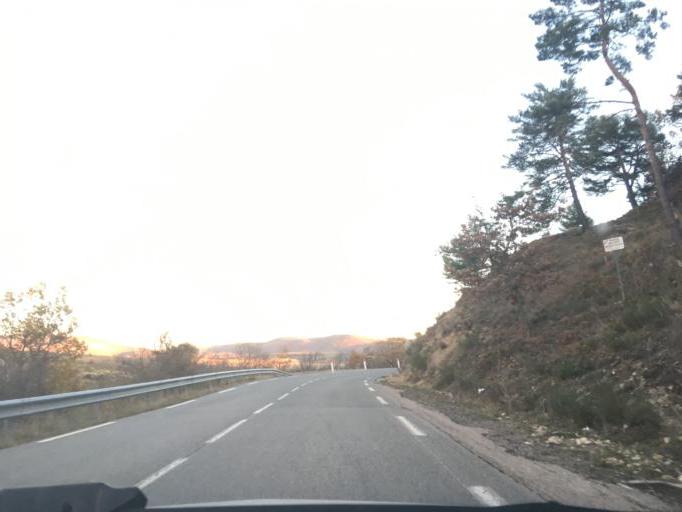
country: FR
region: Provence-Alpes-Cote d'Azur
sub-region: Departement du Var
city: Montferrat
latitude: 43.6967
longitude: 6.5043
